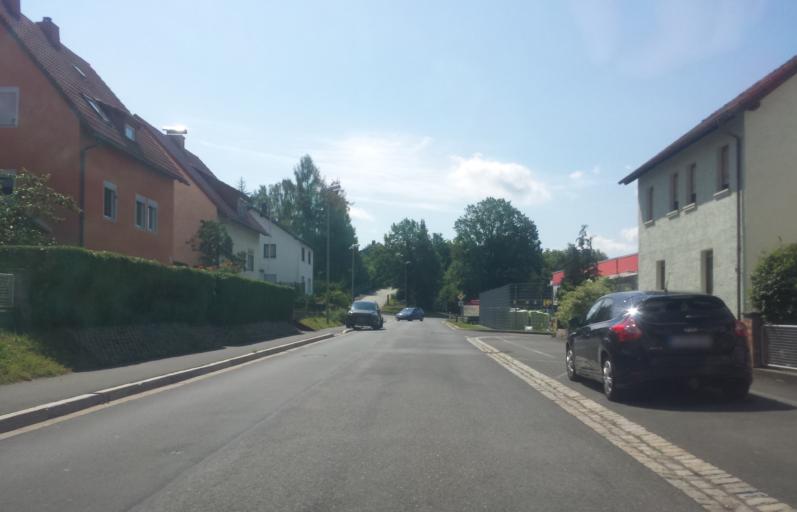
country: DE
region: Bavaria
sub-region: Upper Franconia
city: Burgkunstadt
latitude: 50.1346
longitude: 11.2554
